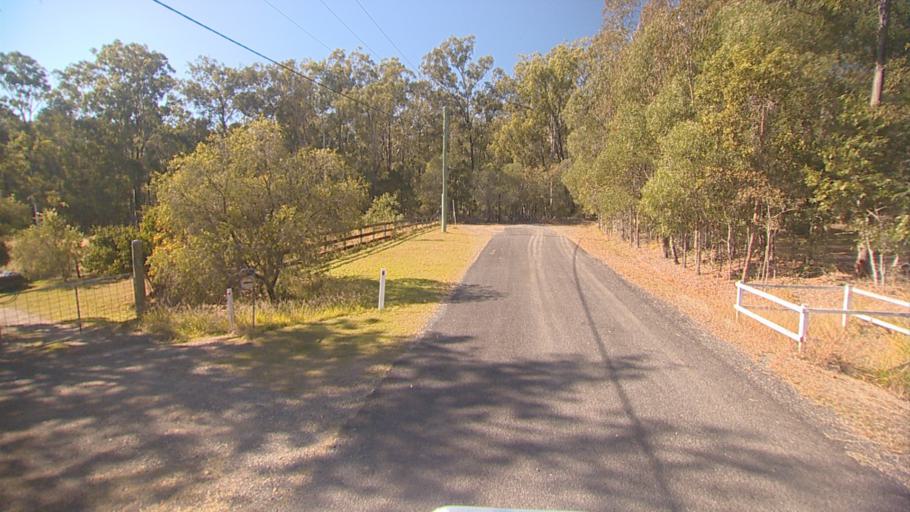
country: AU
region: Queensland
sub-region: Logan
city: Logan Reserve
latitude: -27.7582
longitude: 153.1287
